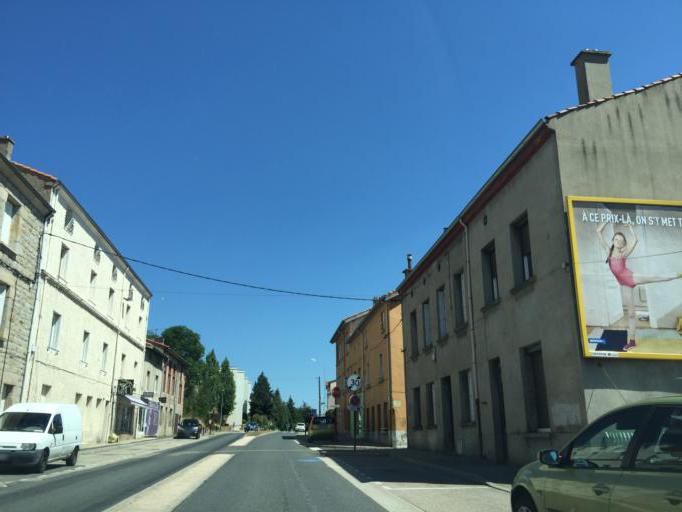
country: FR
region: Rhone-Alpes
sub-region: Departement de la Loire
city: Saint-Jean-Bonnefonds
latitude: 45.4473
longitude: 4.4356
